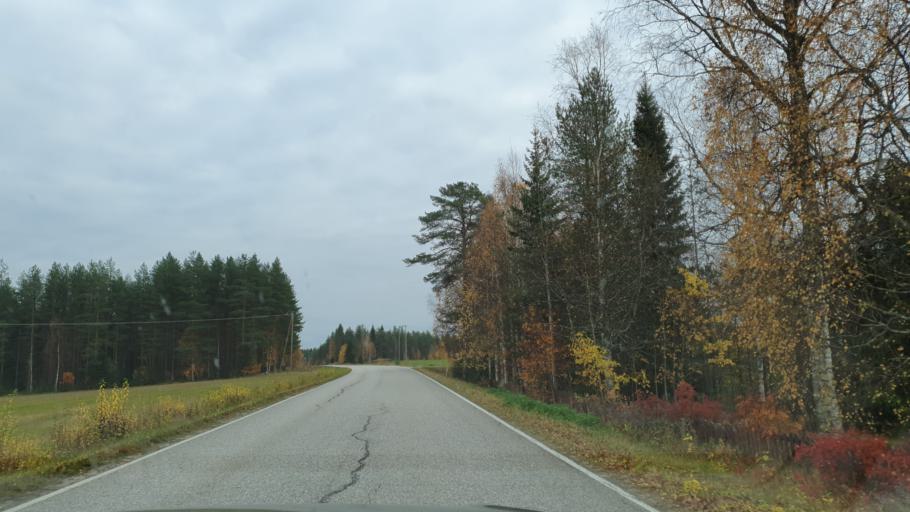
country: FI
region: Kainuu
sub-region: Kajaani
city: Ristijaervi
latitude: 64.4576
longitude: 28.3256
